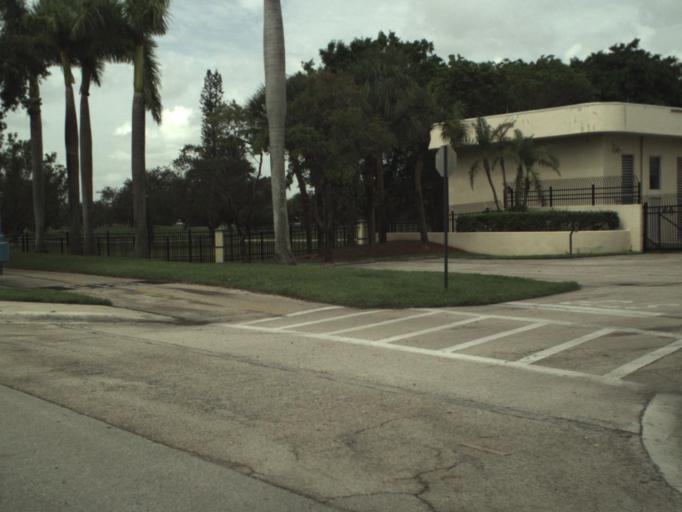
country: US
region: Florida
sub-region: Broward County
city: Kendall Green
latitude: 26.2538
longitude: -80.1006
